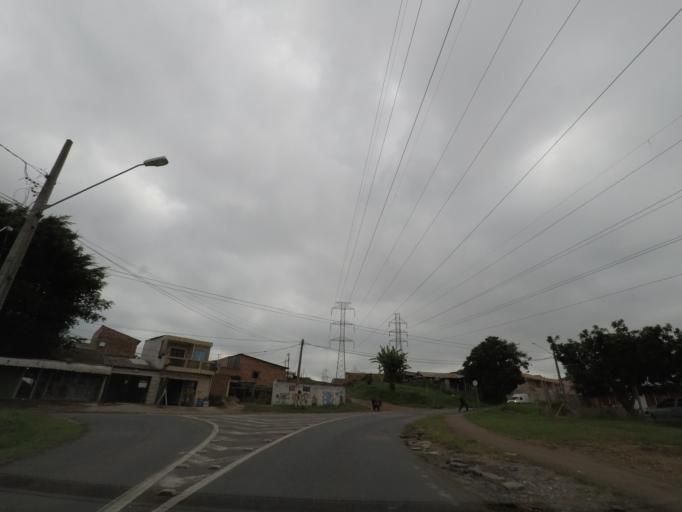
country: BR
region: Parana
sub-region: Curitiba
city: Curitiba
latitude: -25.4664
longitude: -49.3149
